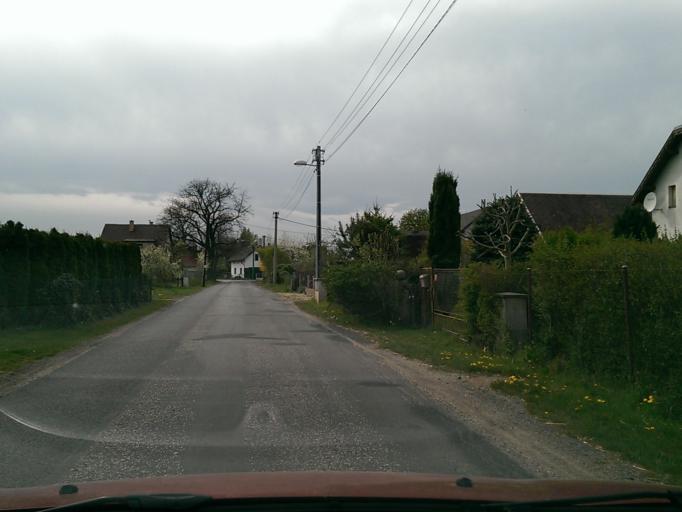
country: CZ
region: Central Bohemia
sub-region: Okres Mlada Boleslav
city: Zd'ar
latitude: 50.5521
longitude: 15.0653
